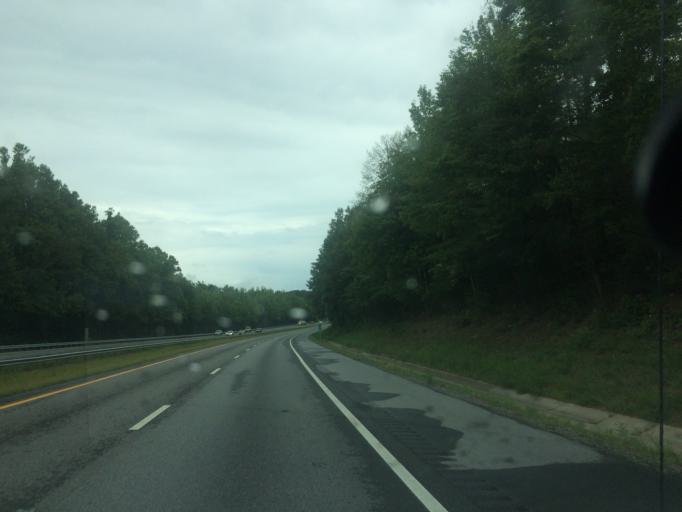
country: US
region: North Carolina
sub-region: Polk County
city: Columbus
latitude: 35.2494
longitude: -82.2094
